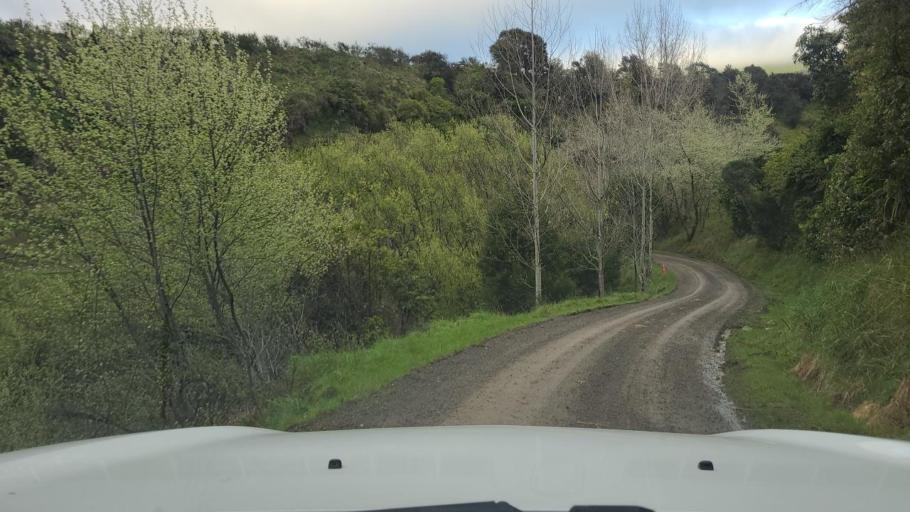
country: NZ
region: Wellington
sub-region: Masterton District
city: Masterton
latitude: -41.1709
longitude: 175.6981
